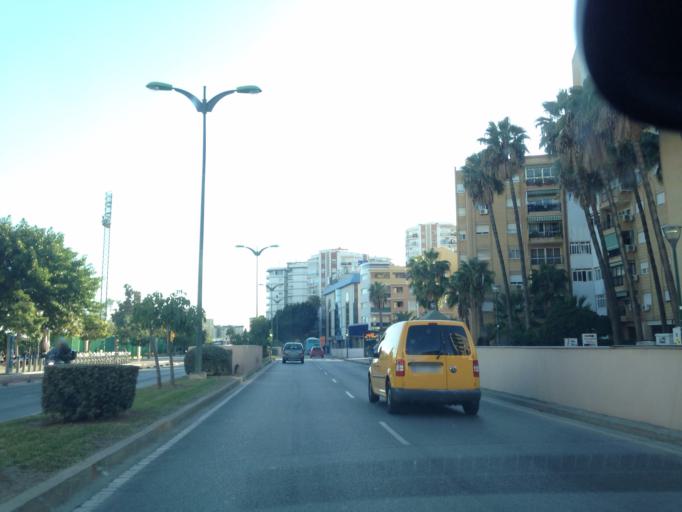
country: ES
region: Andalusia
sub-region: Provincia de Malaga
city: Malaga
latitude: 36.7217
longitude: -4.4490
